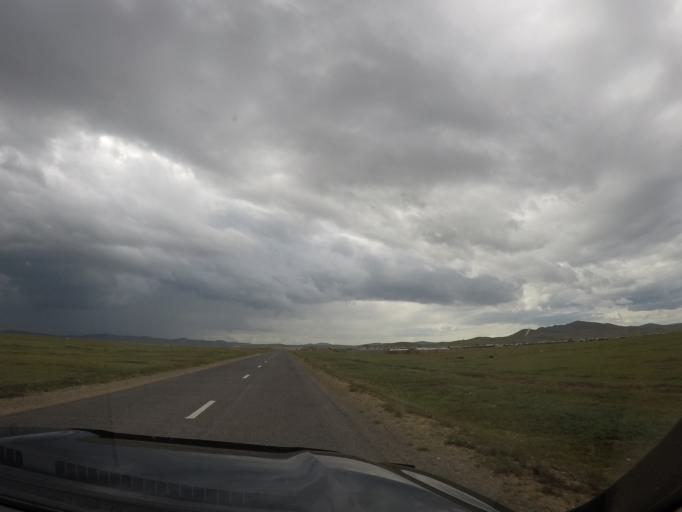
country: MN
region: Hentiy
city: Avraga
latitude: 47.4843
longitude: 109.4850
